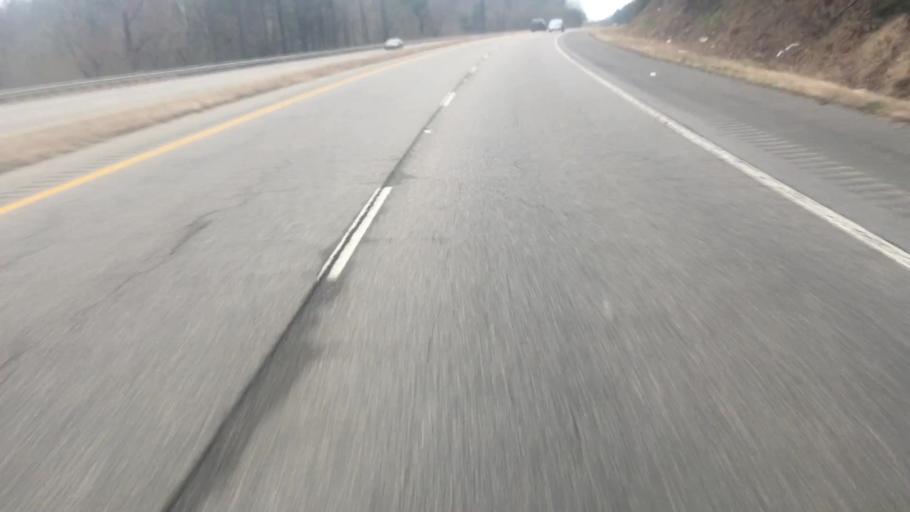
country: US
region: Alabama
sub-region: Walker County
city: Cordova
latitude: 33.8146
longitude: -87.1485
